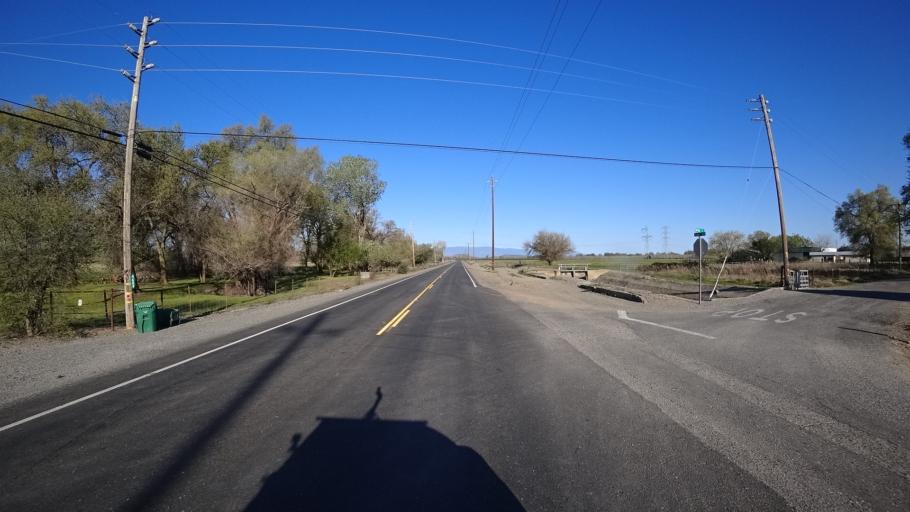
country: US
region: California
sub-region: Glenn County
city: Orland
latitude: 39.7747
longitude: -122.2711
